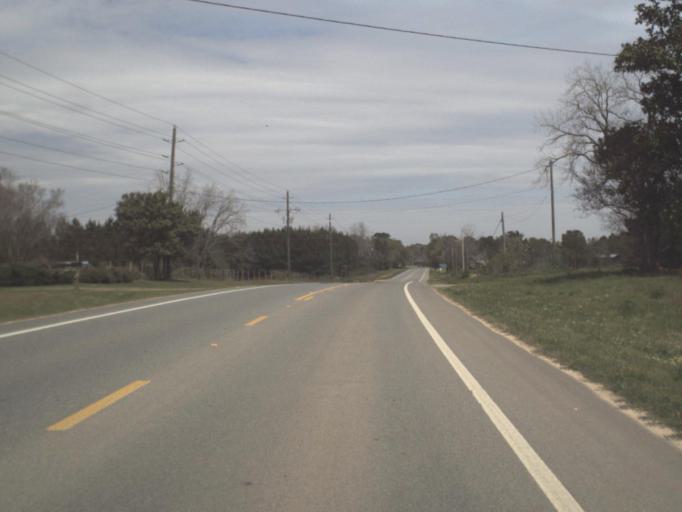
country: US
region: Florida
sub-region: Jackson County
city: Graceville
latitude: 30.9334
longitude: -85.4198
